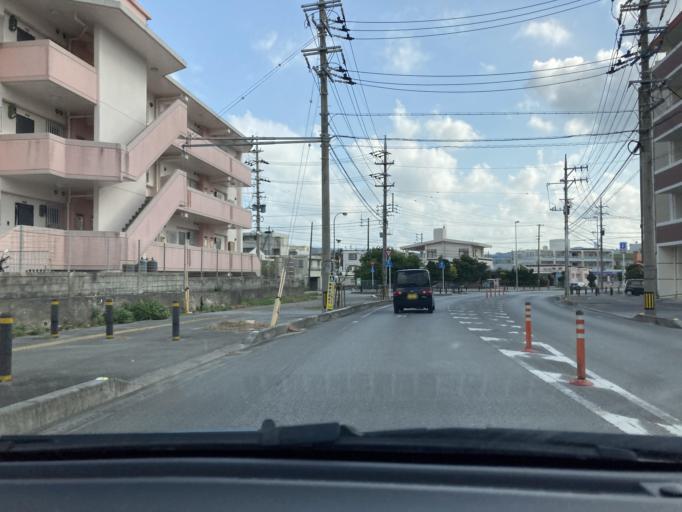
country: JP
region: Okinawa
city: Tomigusuku
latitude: 26.1523
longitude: 127.7176
